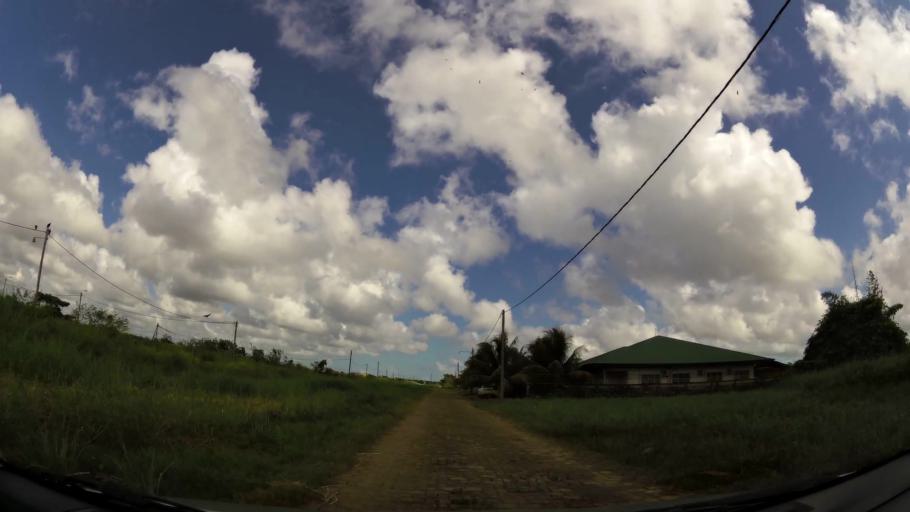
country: SR
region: Commewijne
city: Nieuw Amsterdam
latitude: 5.8681
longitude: -55.1232
